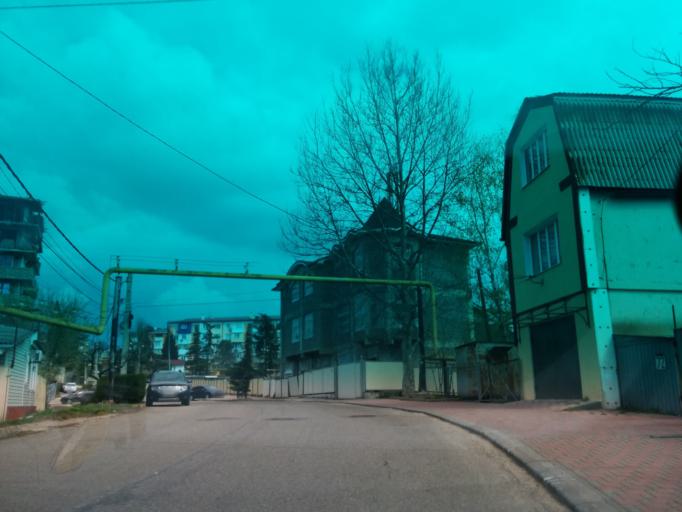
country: RU
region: Krasnodarskiy
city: Tuapse
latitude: 44.1034
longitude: 39.0829
